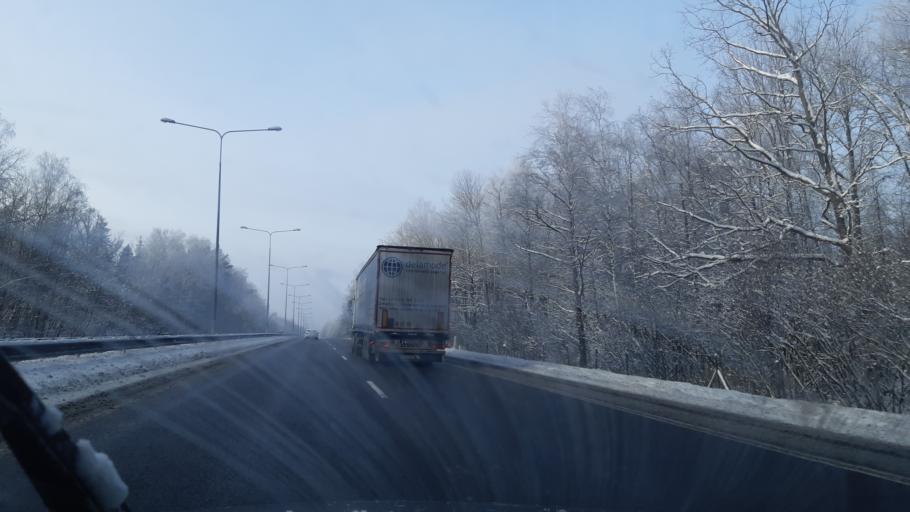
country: LT
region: Kauno apskritis
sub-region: Kauno rajonas
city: Karmelava
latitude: 54.9001
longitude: 24.1374
